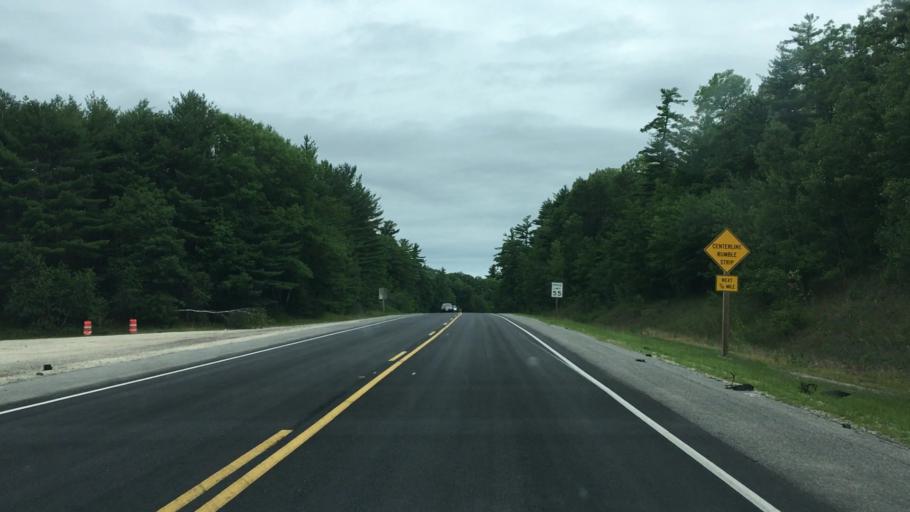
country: US
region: Maine
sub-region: Washington County
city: Cherryfield
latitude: 44.9041
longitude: -67.8565
